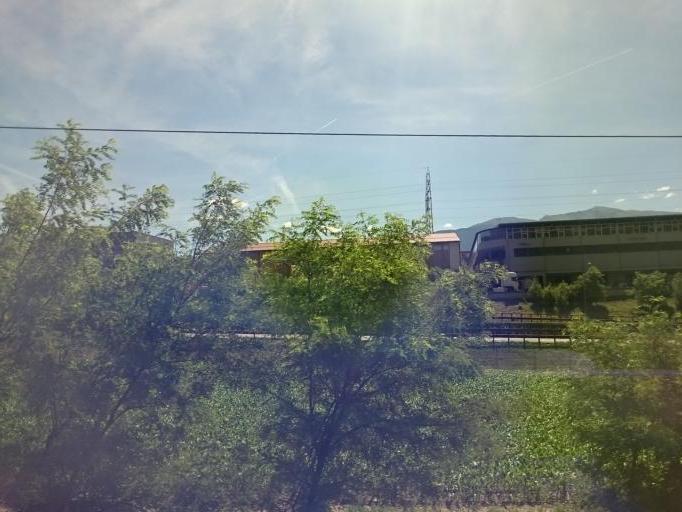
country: IT
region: Trentino-Alto Adige
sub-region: Bolzano
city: Varna
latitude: 46.7616
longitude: 11.6364
